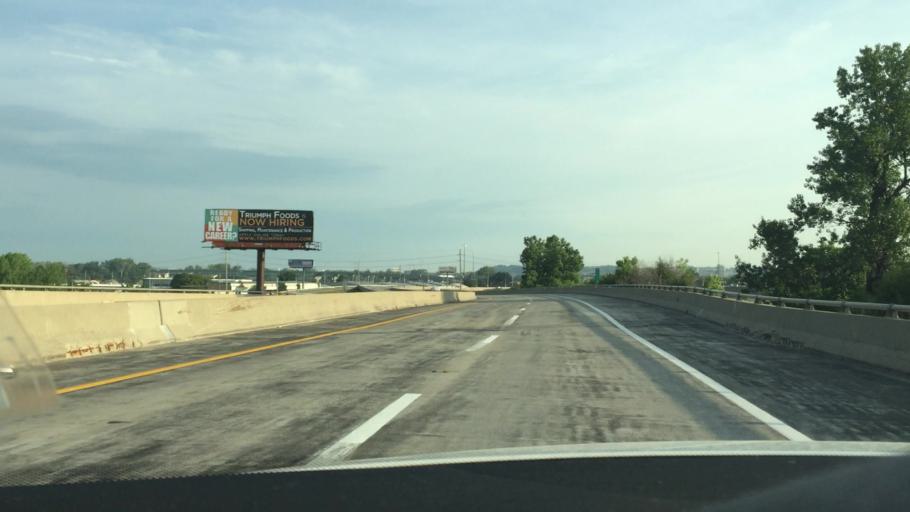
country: US
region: Kansas
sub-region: Doniphan County
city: Elwood
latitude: 39.7386
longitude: -94.8512
